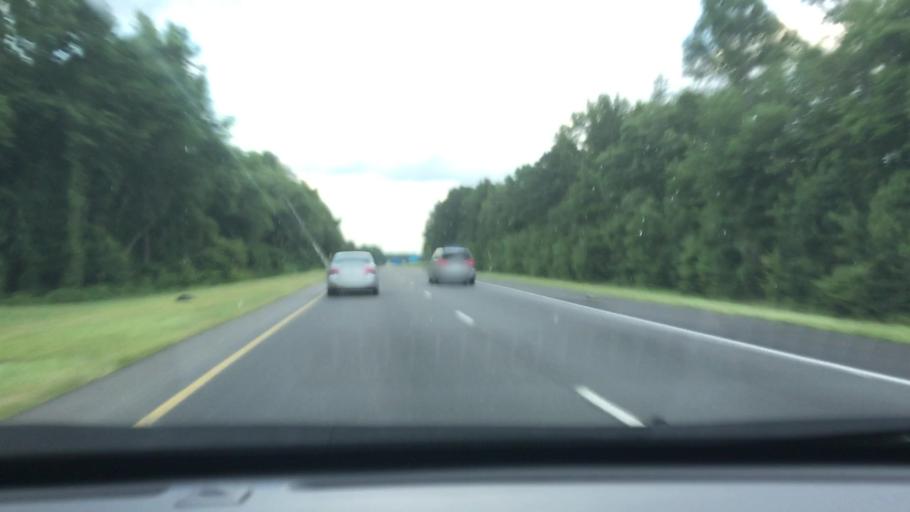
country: US
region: North Carolina
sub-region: Cumberland County
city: Eastover
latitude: 35.0685
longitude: -78.7922
